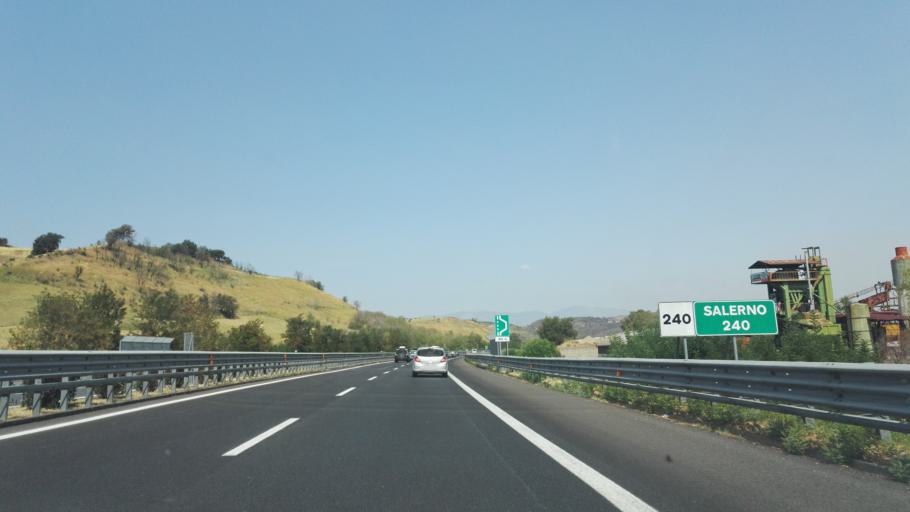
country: IT
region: Calabria
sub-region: Provincia di Cosenza
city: Taverna
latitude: 39.4614
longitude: 16.2242
